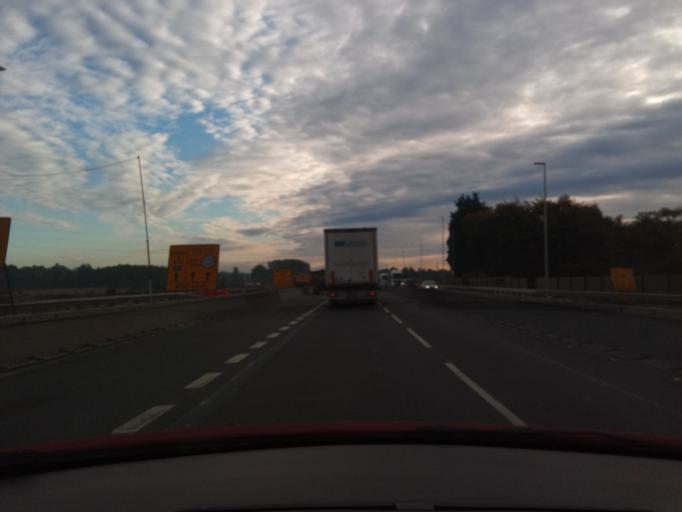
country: GB
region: England
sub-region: Cambridgeshire
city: Histon
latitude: 52.2344
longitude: 0.1021
